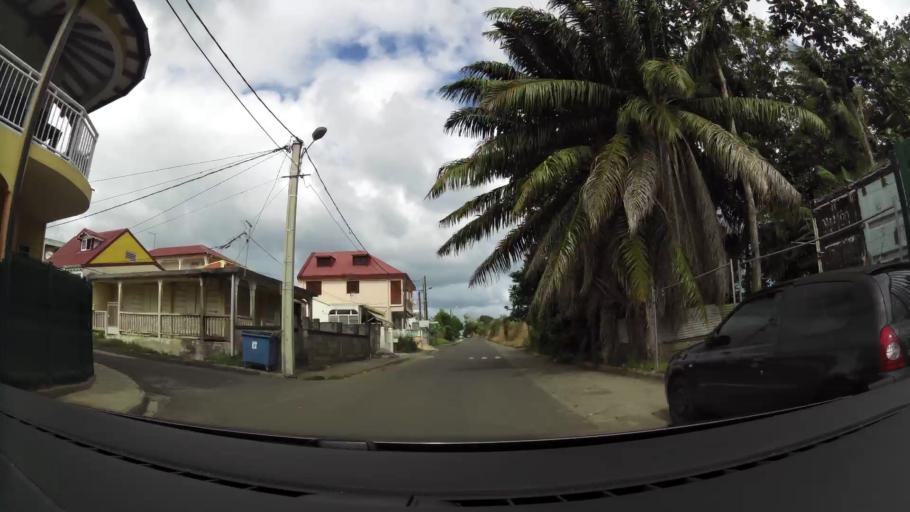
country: GP
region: Guadeloupe
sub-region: Guadeloupe
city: Baie-Mahault
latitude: 16.2674
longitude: -61.5834
